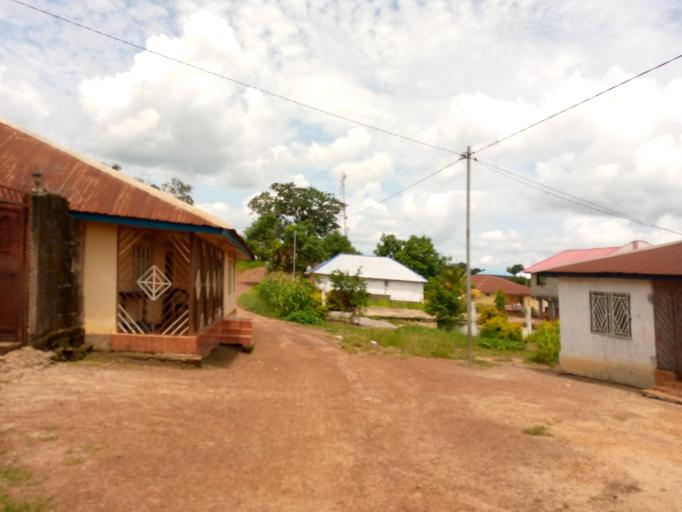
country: SL
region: Northern Province
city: Magburaka
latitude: 8.7247
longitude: -11.9359
